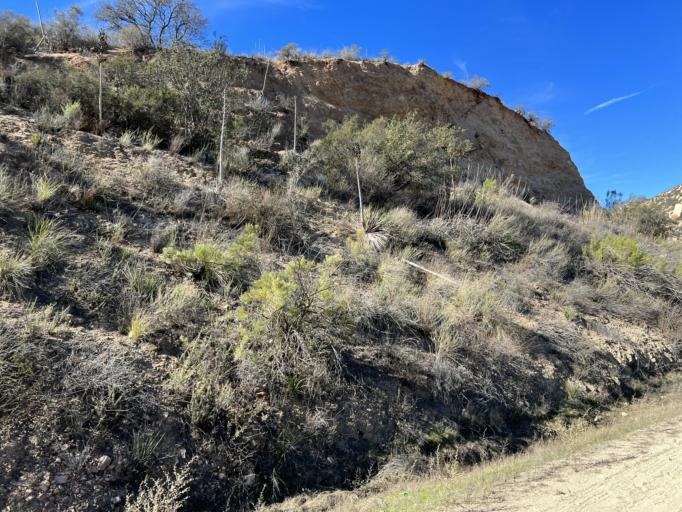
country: US
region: California
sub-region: San Diego County
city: Poway
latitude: 33.0262
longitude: -116.9989
